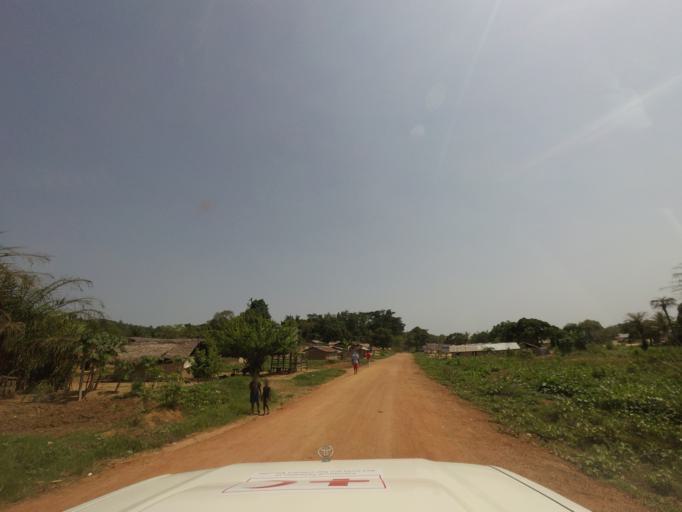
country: GN
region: Nzerekore
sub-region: Yomou
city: Yomou
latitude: 7.3392
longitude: -9.5002
